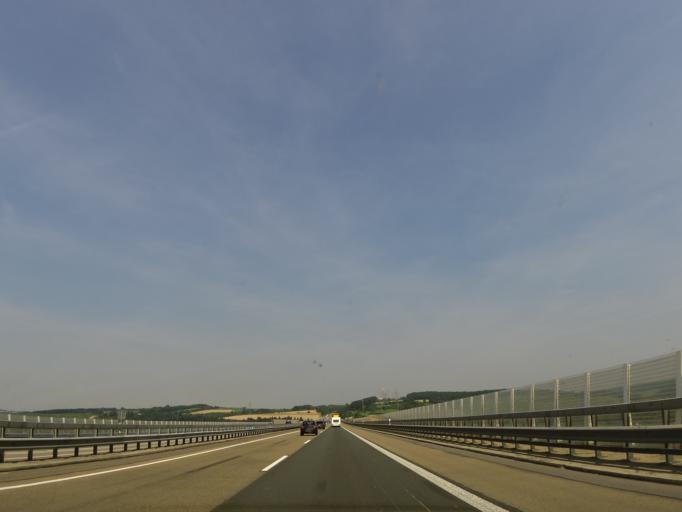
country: DE
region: Rheinland-Pfalz
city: Schalkenbach
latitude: 50.5427
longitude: 7.1646
